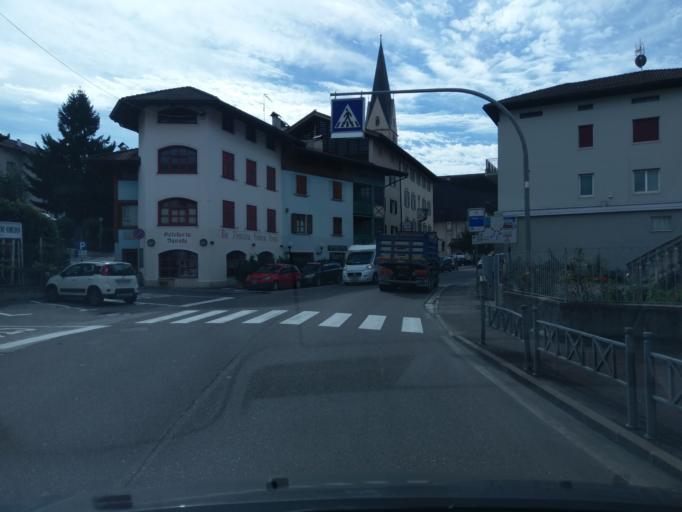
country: IT
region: Trentino-Alto Adige
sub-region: Provincia di Trento
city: Cles
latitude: 46.3657
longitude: 11.0358
